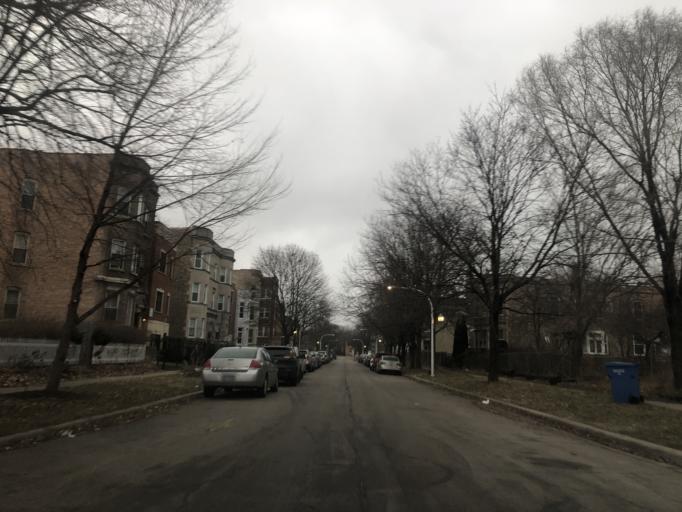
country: US
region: Illinois
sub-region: Cook County
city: Chicago
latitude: 41.7781
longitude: -87.6004
